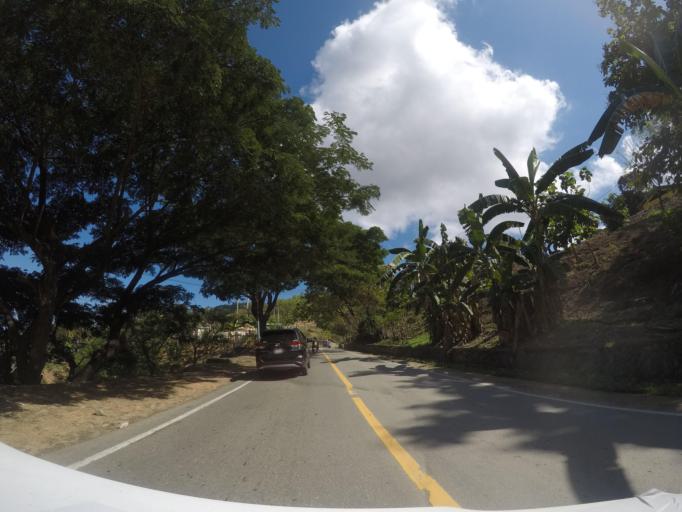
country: TL
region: Dili
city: Dili
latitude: -8.5661
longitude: 125.6312
